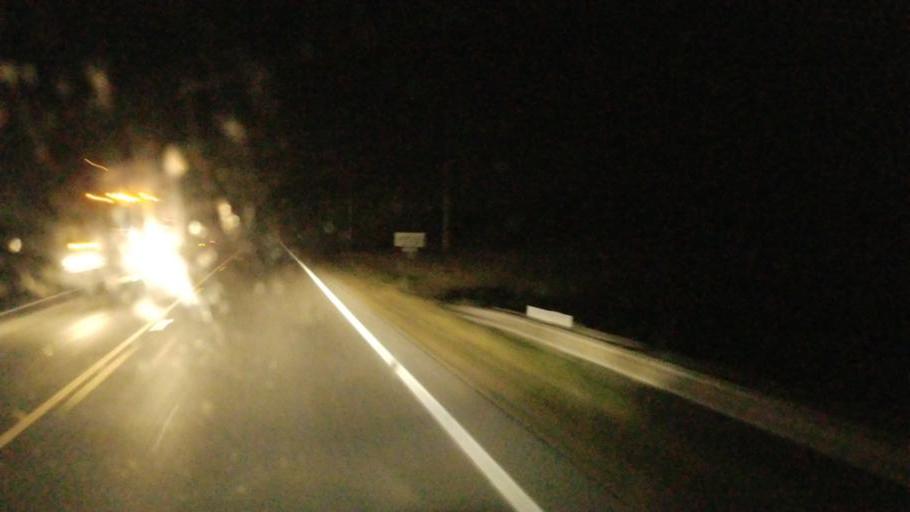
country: US
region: Ohio
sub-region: Hardin County
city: Kenton
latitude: 40.5505
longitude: -83.5338
